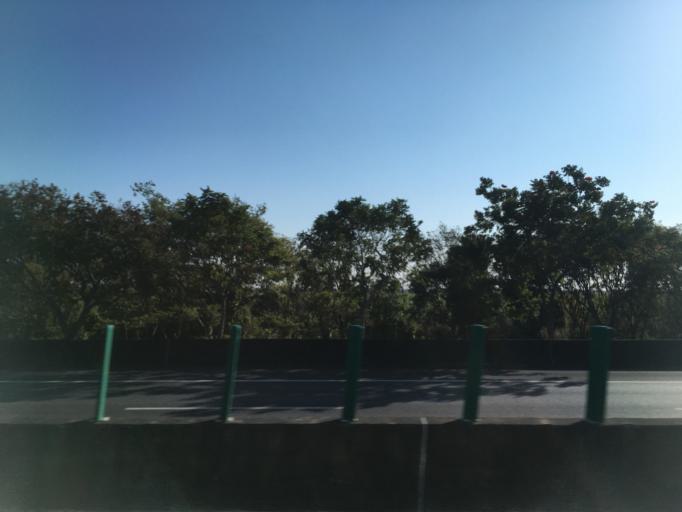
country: TW
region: Taiwan
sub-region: Chiayi
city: Taibao
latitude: 23.4283
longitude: 120.3345
